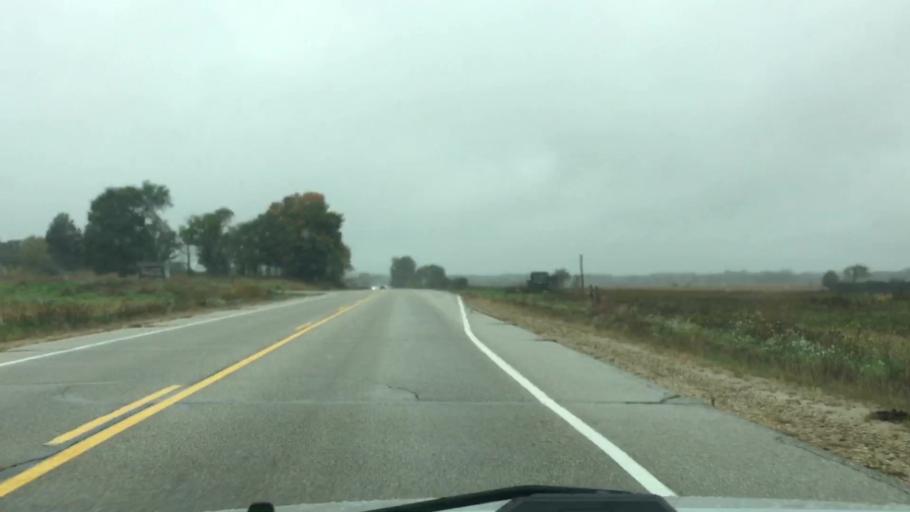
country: US
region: Wisconsin
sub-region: Waukesha County
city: Eagle
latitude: 42.8792
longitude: -88.5234
